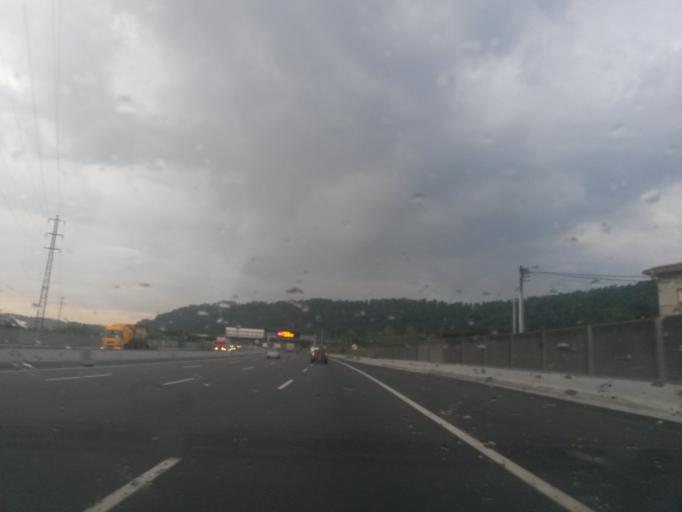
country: ES
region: Catalonia
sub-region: Provincia de Girona
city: Sarria de Ter
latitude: 42.0261
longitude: 2.8214
